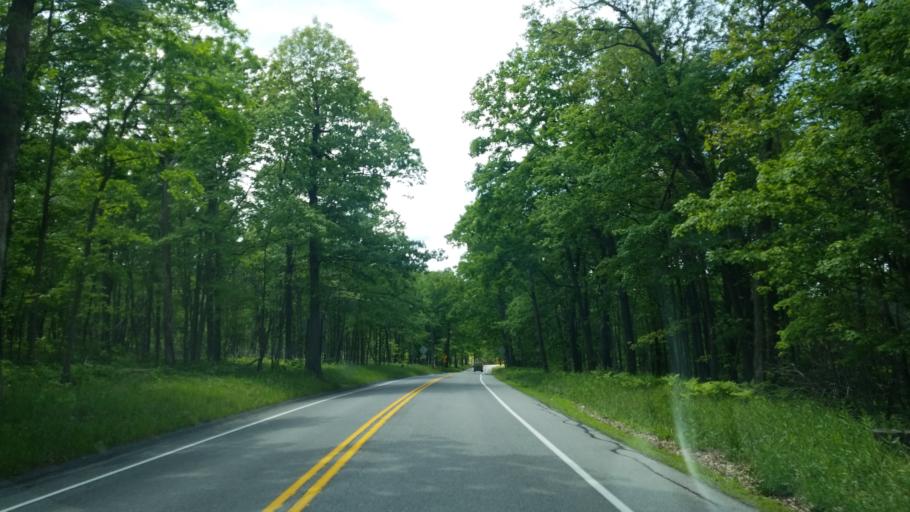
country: US
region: Pennsylvania
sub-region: Blair County
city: Tipton
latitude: 40.7013
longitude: -78.3006
